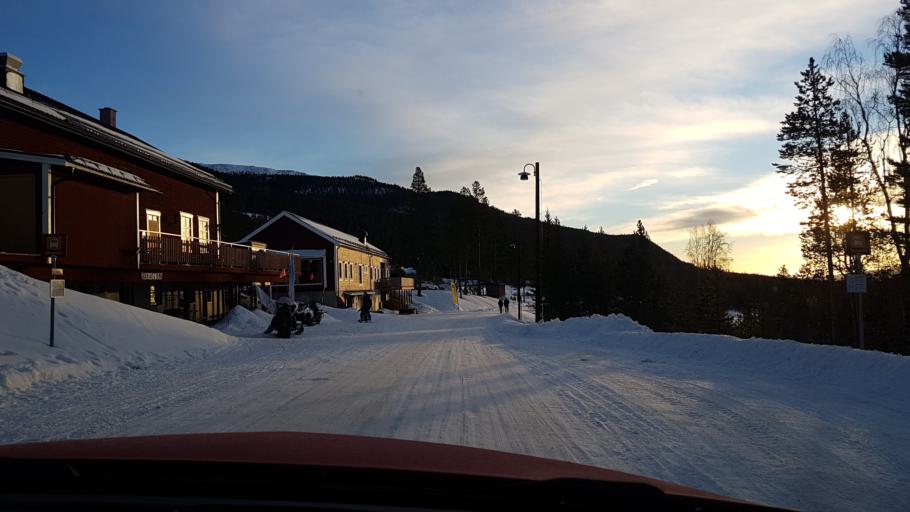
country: SE
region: Jaemtland
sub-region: Harjedalens Kommun
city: Sveg
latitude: 62.4159
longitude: 13.9492
